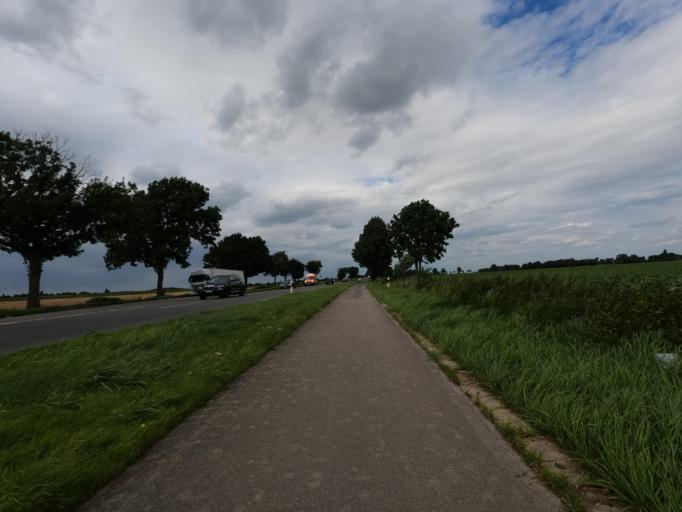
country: DE
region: North Rhine-Westphalia
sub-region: Regierungsbezirk Koln
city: Ubach-Palenberg
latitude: 50.9353
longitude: 6.1335
